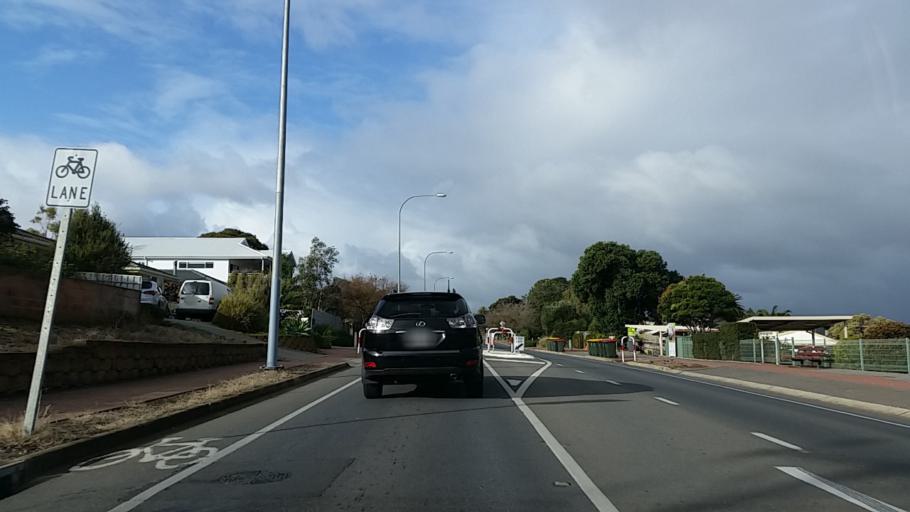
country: AU
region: South Australia
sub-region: Adelaide
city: Port Noarlunga
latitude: -35.1464
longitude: 138.4793
